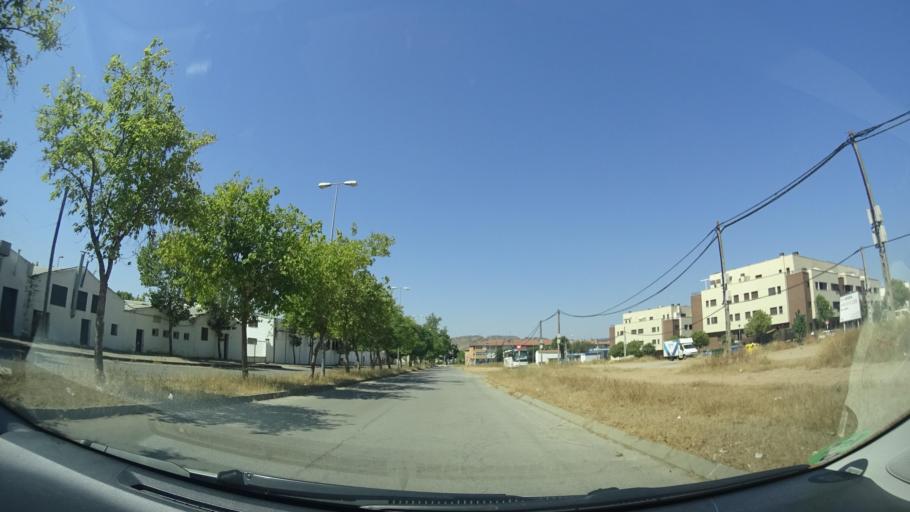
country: ES
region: Extremadura
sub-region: Provincia de Badajoz
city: Zafra
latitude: 38.4300
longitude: -6.4112
